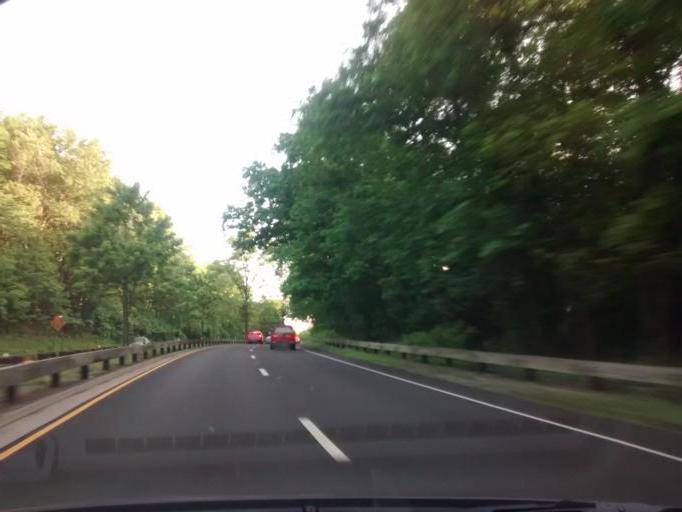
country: US
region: Connecticut
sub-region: Fairfield County
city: Glenville
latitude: 41.0817
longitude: -73.6660
